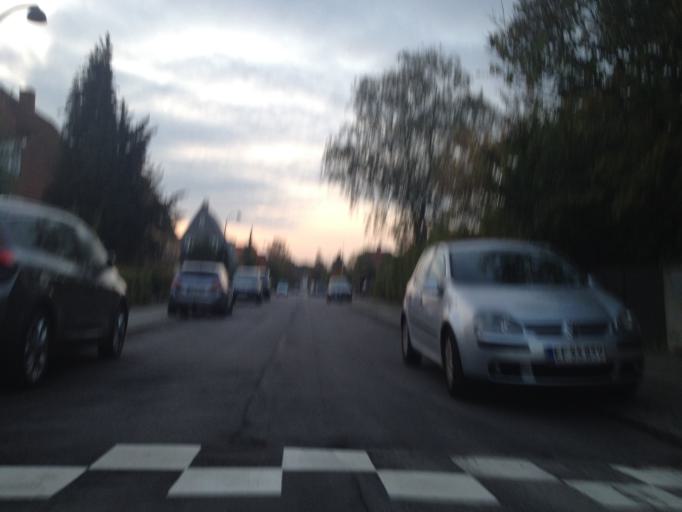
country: DK
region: Capital Region
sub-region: Gentofte Kommune
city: Charlottenlund
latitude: 55.7458
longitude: 12.5619
